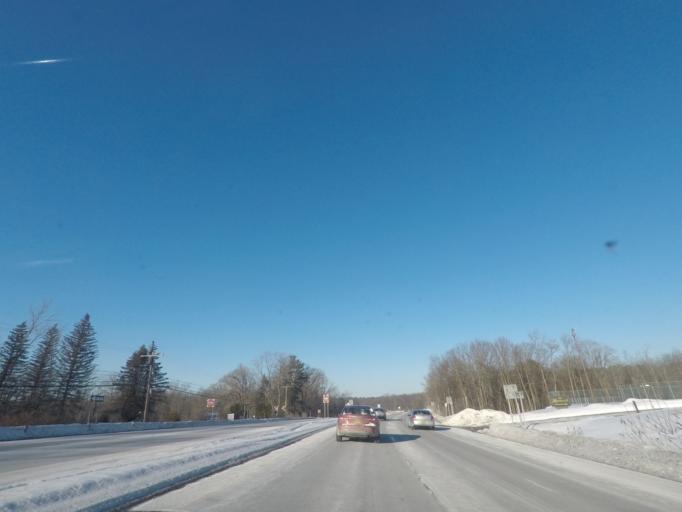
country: US
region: New York
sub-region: Saratoga County
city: Saratoga Springs
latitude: 43.0280
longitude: -73.7922
